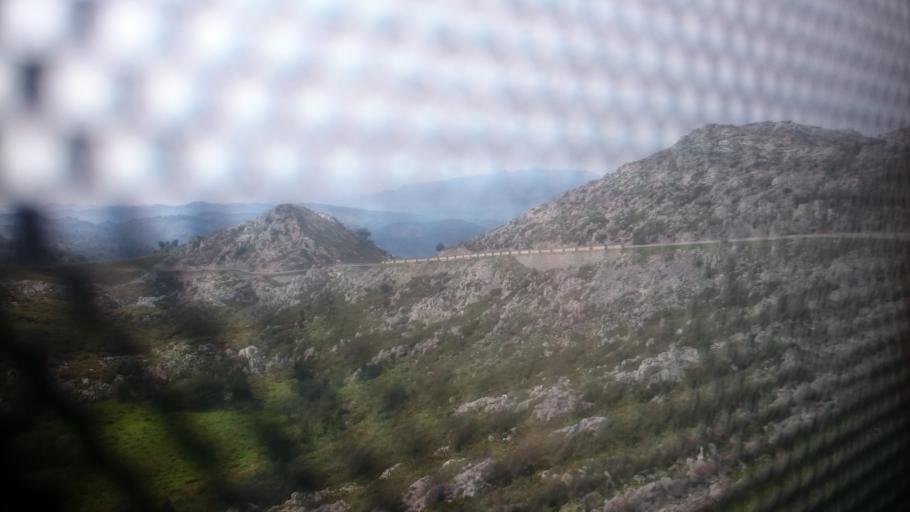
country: ES
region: Asturias
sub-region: Province of Asturias
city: Amieva
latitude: 43.2894
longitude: -5.0047
